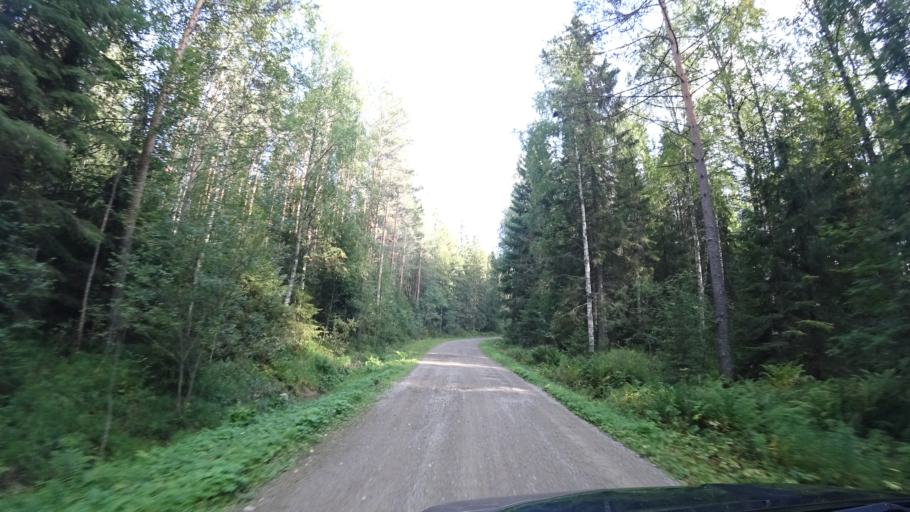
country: FI
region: Paijanne Tavastia
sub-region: Lahti
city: Auttoinen
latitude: 61.2192
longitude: 25.1497
